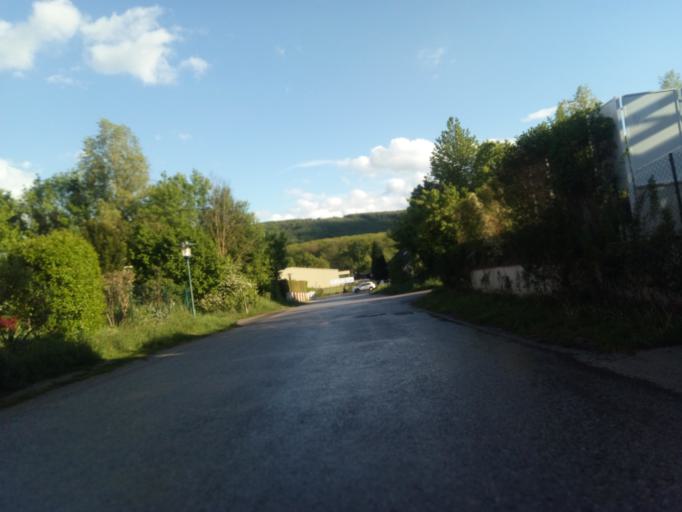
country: AT
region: Lower Austria
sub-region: Politischer Bezirk Modling
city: Kaltenleutgeben
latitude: 48.1368
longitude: 16.1885
